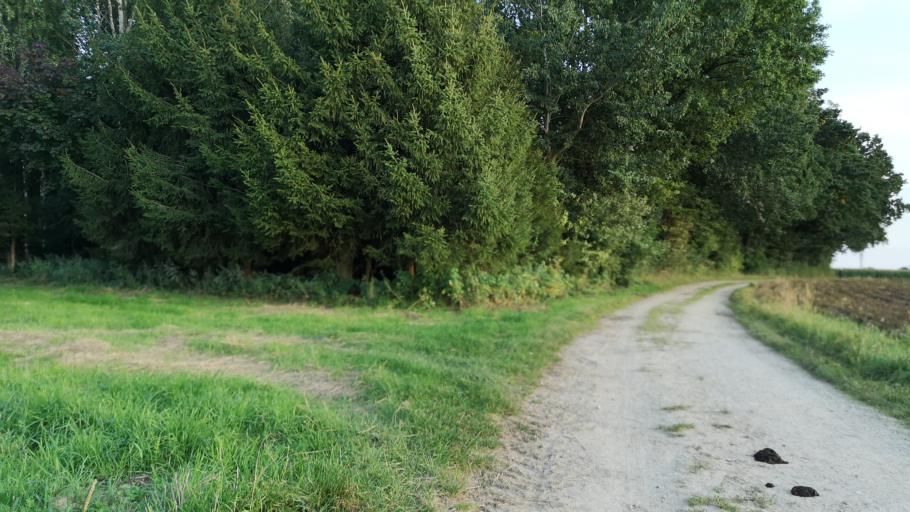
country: DE
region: Bavaria
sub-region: Upper Bavaria
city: Poing
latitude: 48.1618
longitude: 11.8226
